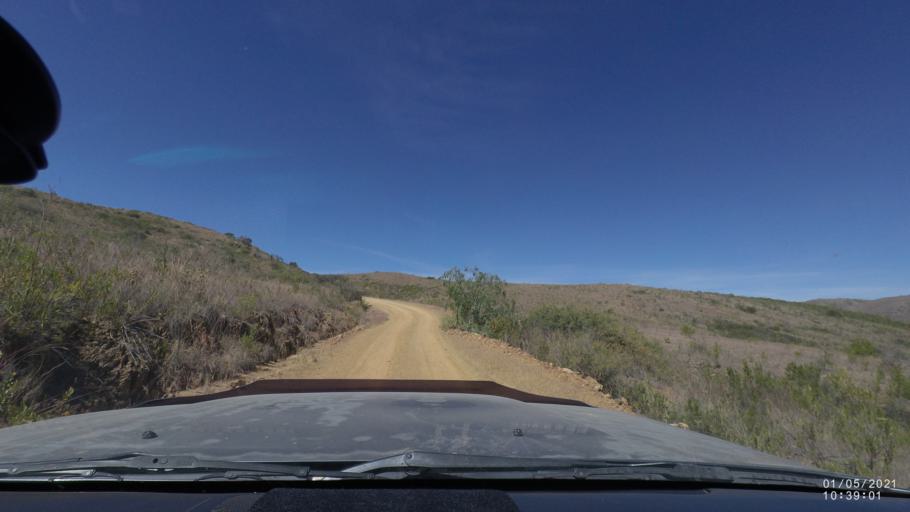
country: BO
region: Cochabamba
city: Capinota
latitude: -17.6050
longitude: -66.1847
